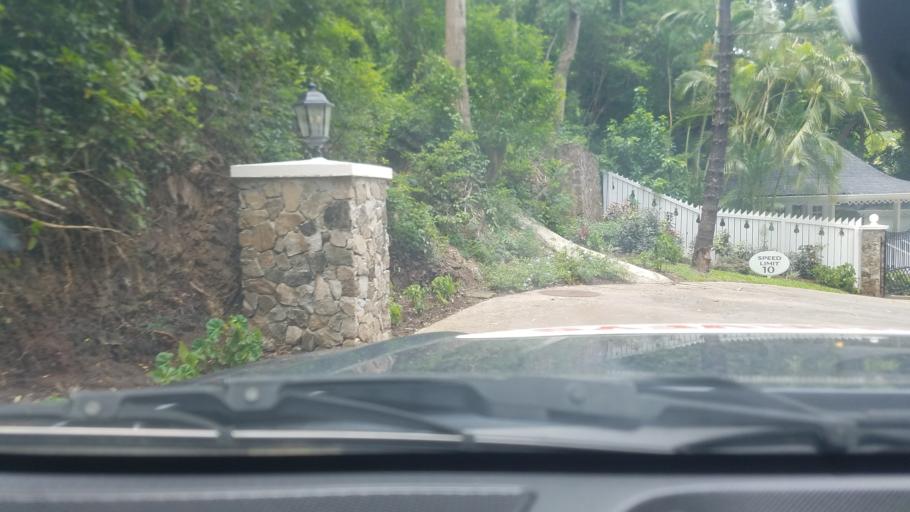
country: LC
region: Soufriere
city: Soufriere
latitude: 13.8346
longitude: -61.0585
